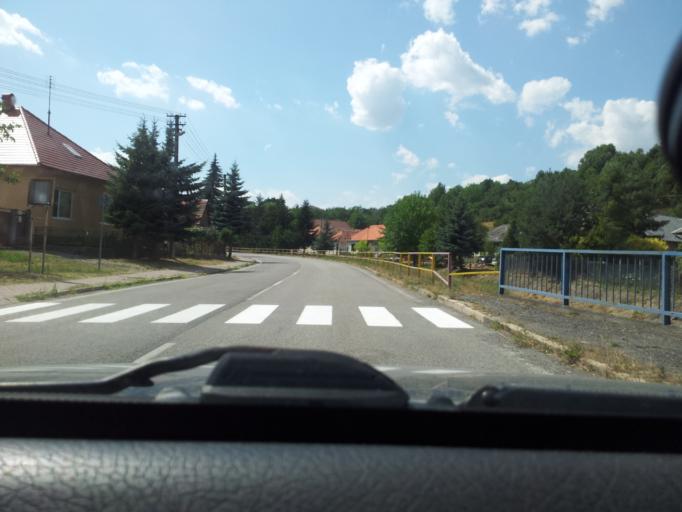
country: SK
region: Nitriansky
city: Tlmace
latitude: 48.3462
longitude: 18.5562
